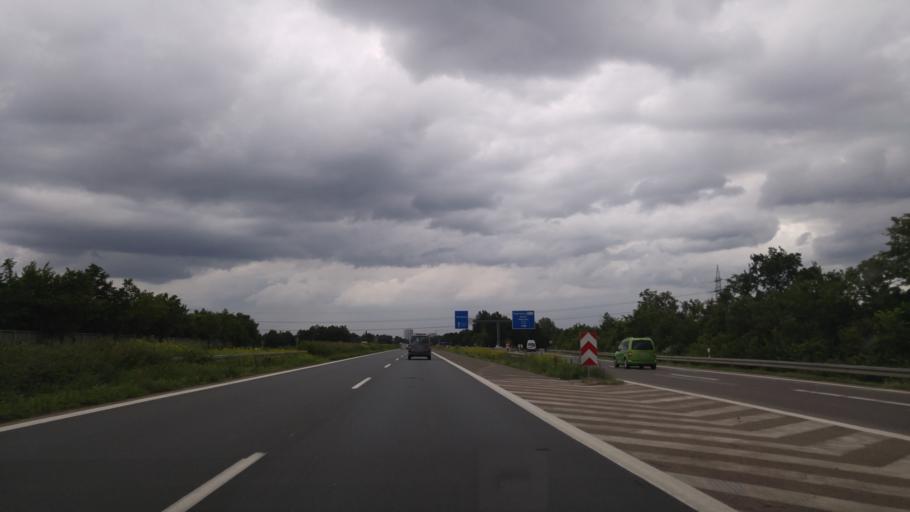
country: DE
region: Bavaria
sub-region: Regierungsbezirk Mittelfranken
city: Erlangen
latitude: 49.5550
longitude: 10.9927
